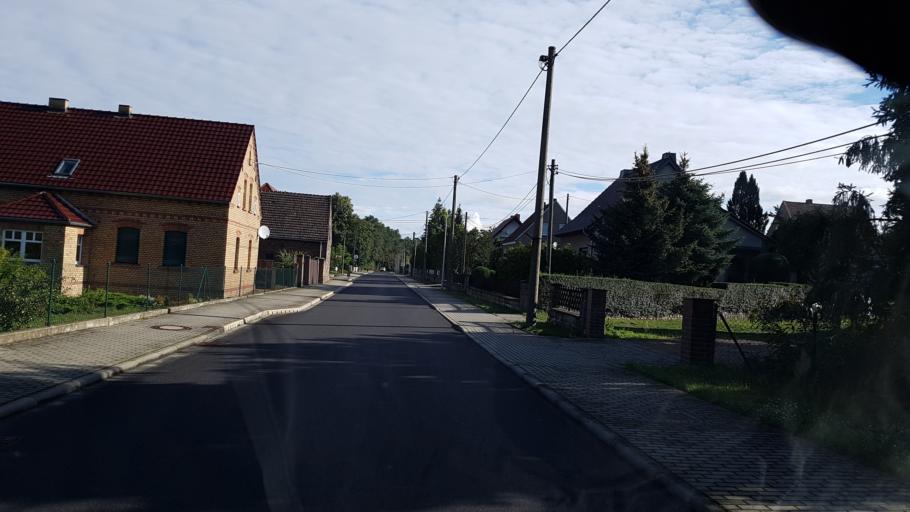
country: DE
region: Saxony
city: Gross Duben
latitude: 51.6250
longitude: 14.5415
